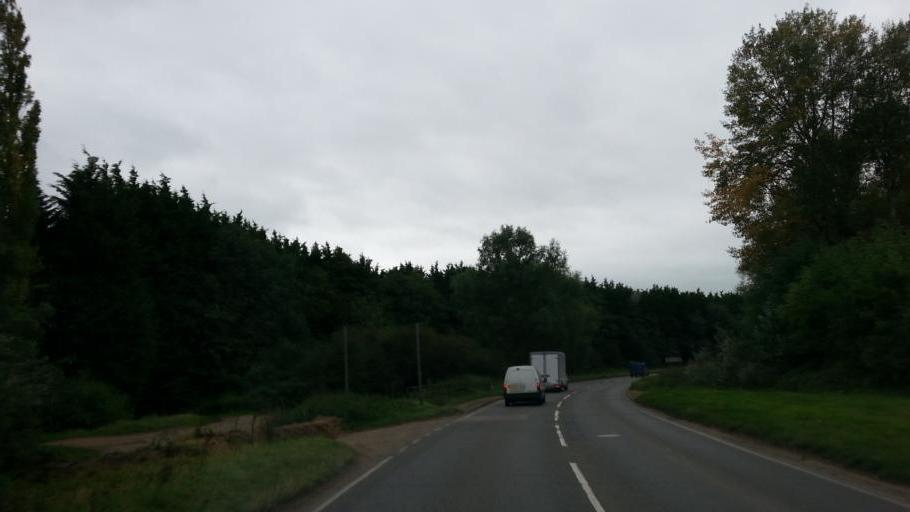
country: GB
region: England
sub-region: Cambridgeshire
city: Hemingford Grey
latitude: 52.3088
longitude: -0.0862
